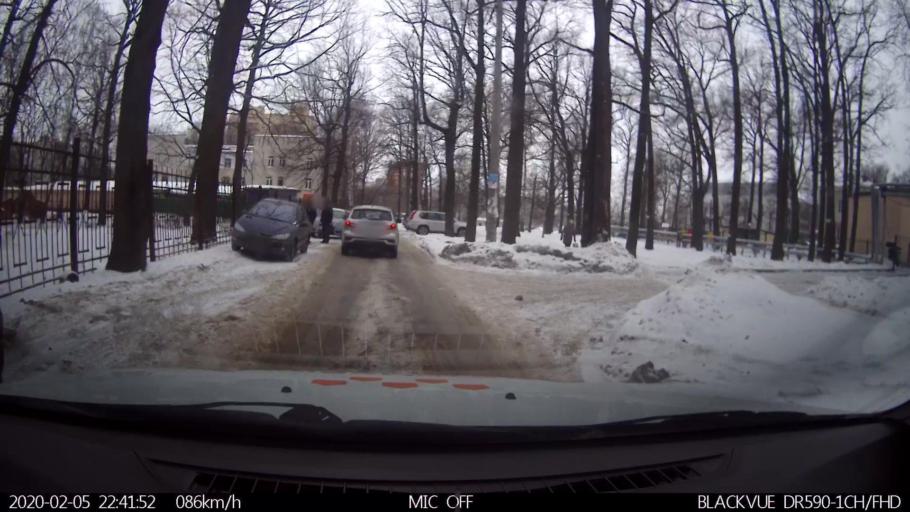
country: RU
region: Nizjnij Novgorod
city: Imeni Stepana Razina
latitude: 54.7197
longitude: 44.3463
